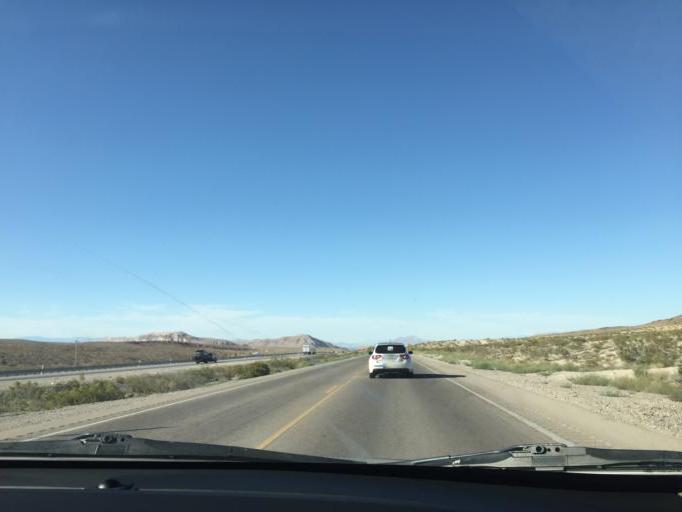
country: US
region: Nevada
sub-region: Clark County
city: Enterprise
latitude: 35.8889
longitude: -115.2217
